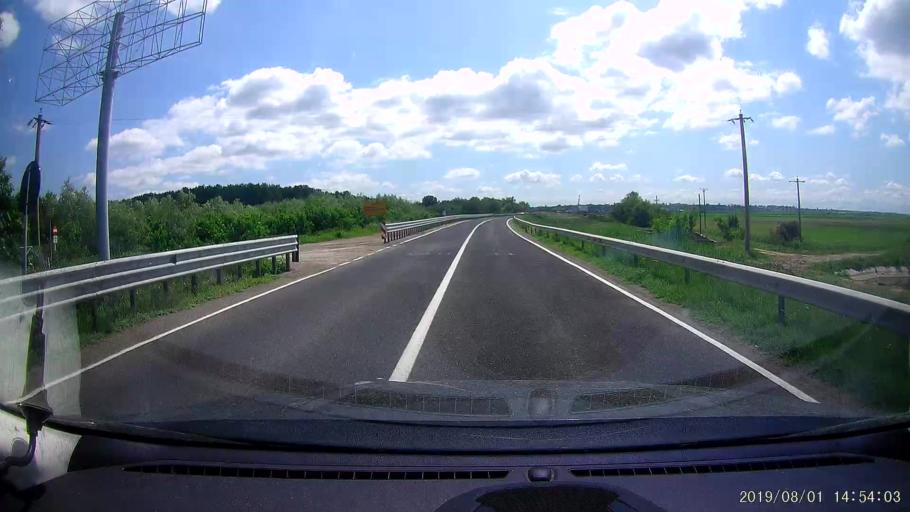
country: RO
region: Braila
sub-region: Municipiul Braila
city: Braila
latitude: 45.3241
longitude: 27.9953
